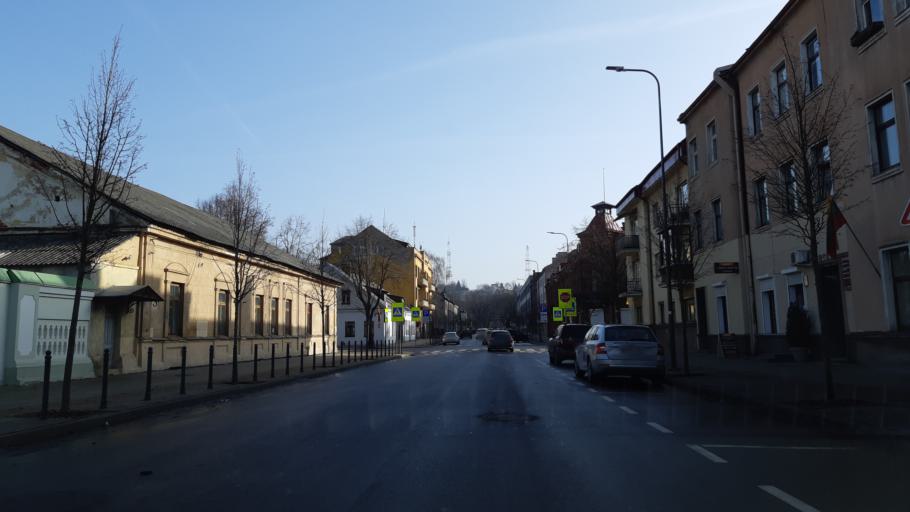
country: LT
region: Kauno apskritis
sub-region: Kaunas
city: Kaunas
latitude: 54.8938
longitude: 23.9200
